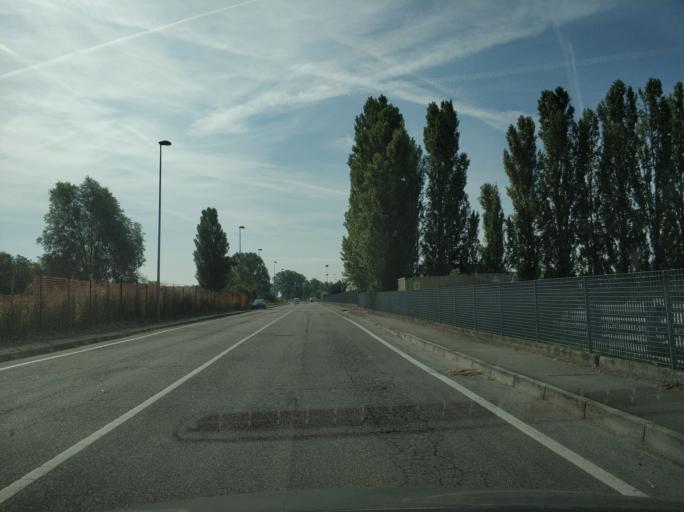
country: IT
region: Veneto
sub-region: Provincia di Padova
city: Este
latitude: 45.2155
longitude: 11.6779
